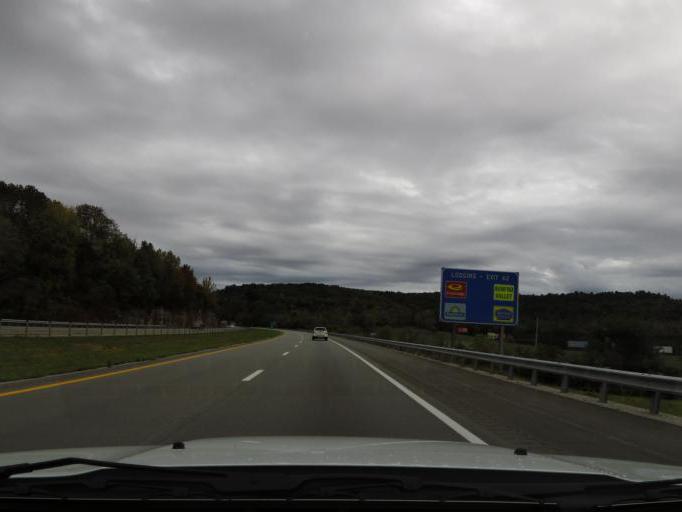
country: US
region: Kentucky
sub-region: Rockcastle County
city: Mount Vernon
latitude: 37.3594
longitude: -84.3077
